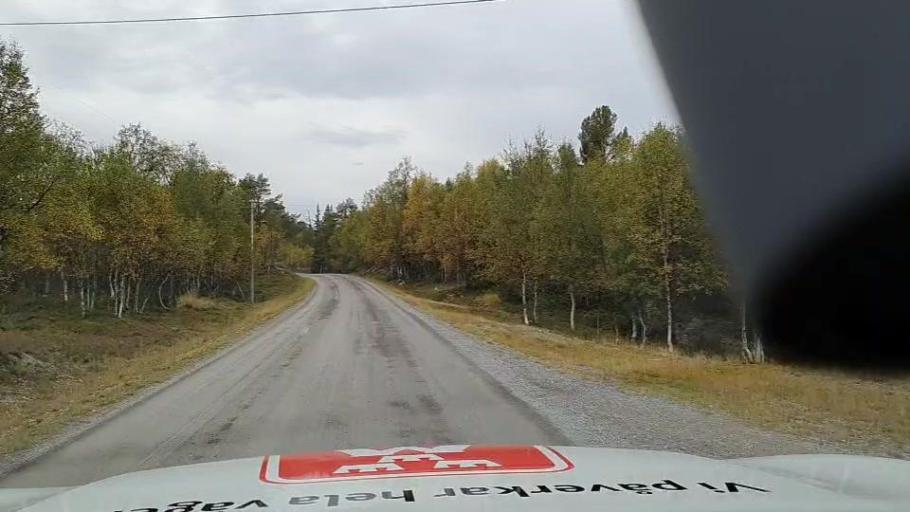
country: NO
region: Hedmark
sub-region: Engerdal
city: Engerdal
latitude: 62.0879
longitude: 12.7536
